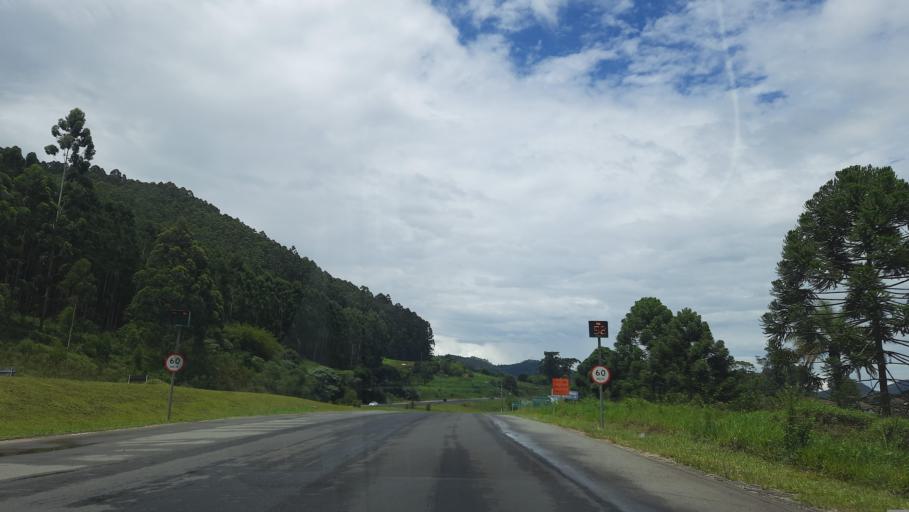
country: BR
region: Minas Gerais
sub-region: Pocos De Caldas
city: Pocos de Caldas
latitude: -21.8000
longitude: -46.6489
